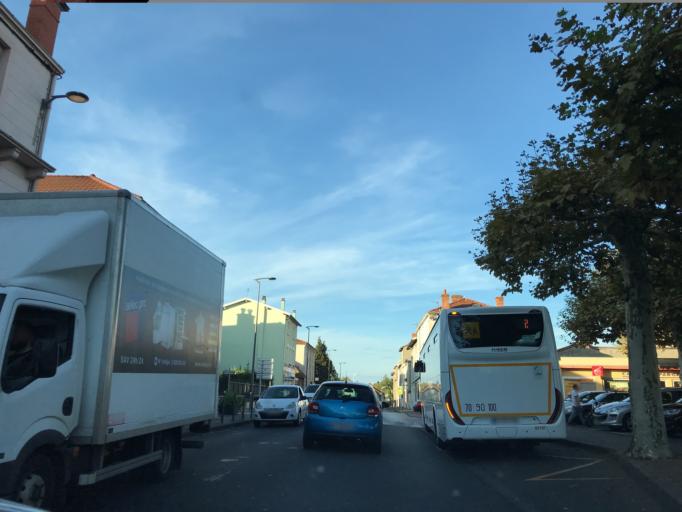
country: FR
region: Auvergne
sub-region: Departement du Puy-de-Dome
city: Puy-Guillaume
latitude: 45.9600
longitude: 3.4741
